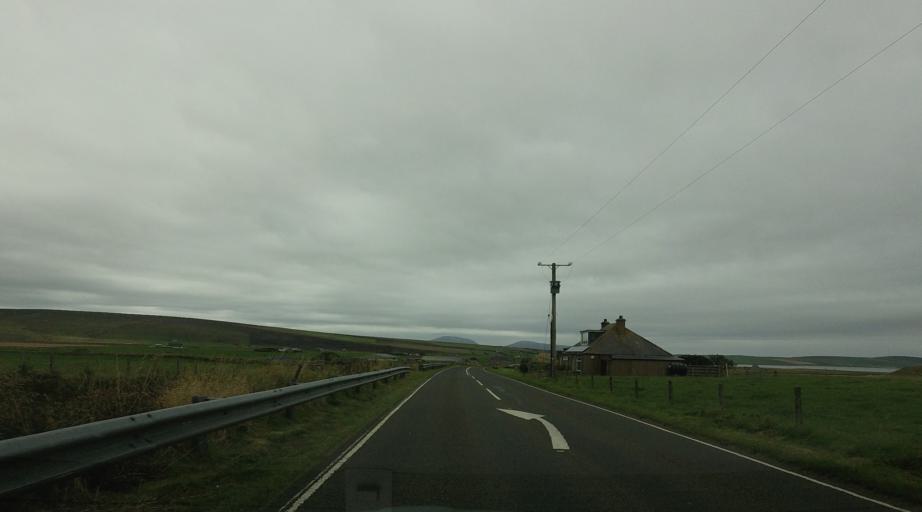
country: GB
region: Scotland
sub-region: Orkney Islands
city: Stromness
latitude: 58.9968
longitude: -3.1818
